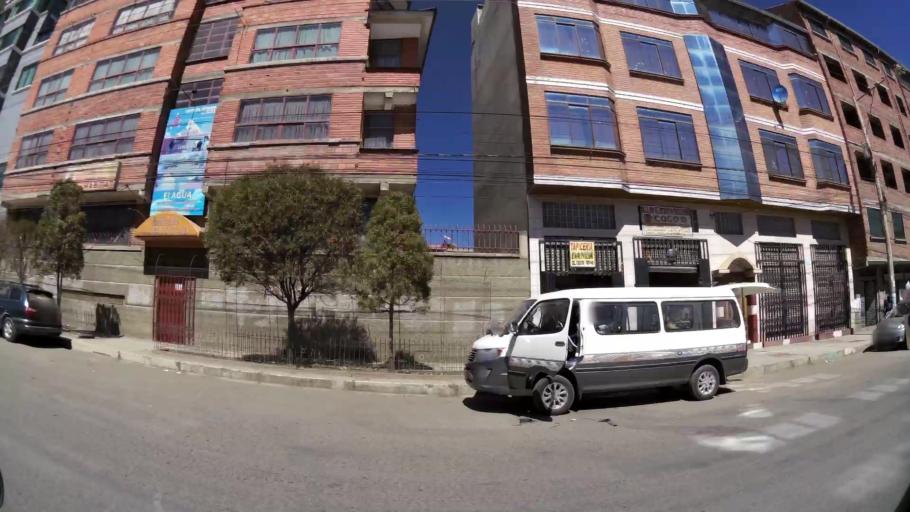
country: BO
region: La Paz
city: La Paz
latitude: -16.4952
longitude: -68.1924
